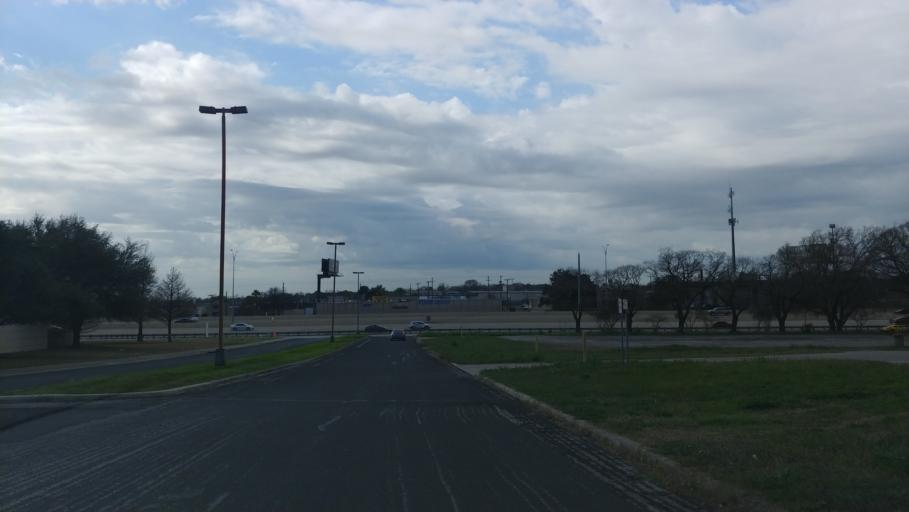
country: US
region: Texas
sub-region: Bexar County
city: Balcones Heights
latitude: 29.4869
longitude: -98.5404
